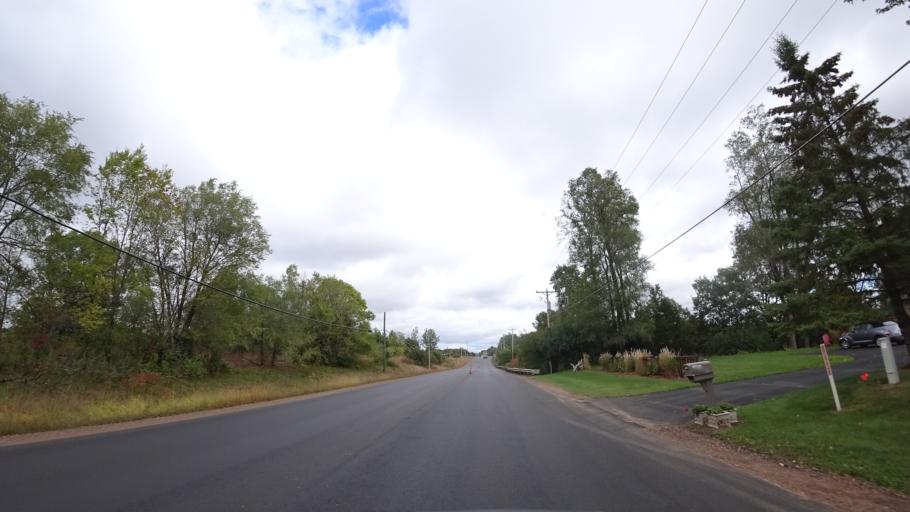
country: US
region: Wisconsin
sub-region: Chippewa County
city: Lake Wissota
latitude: 44.9275
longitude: -91.2943
